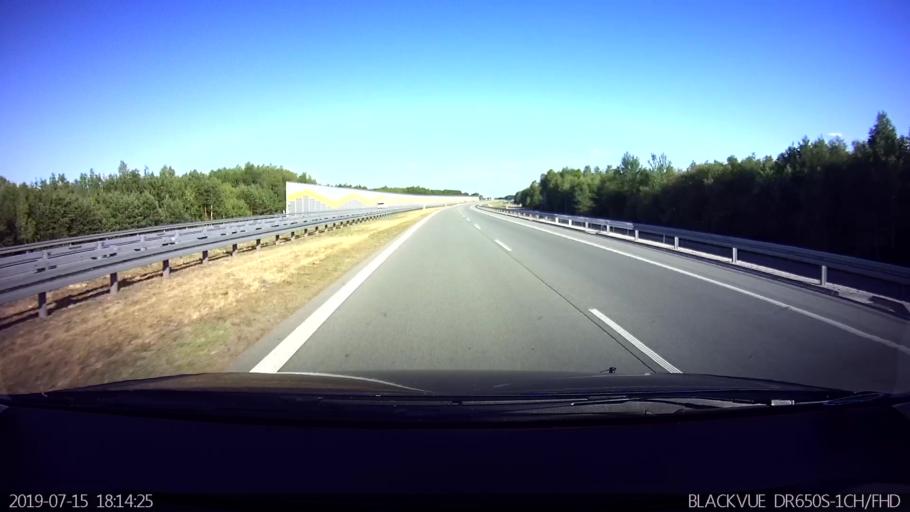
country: PL
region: Lodz Voivodeship
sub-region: Powiat zdunskowolski
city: Zapolice
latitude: 51.5925
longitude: 18.8878
